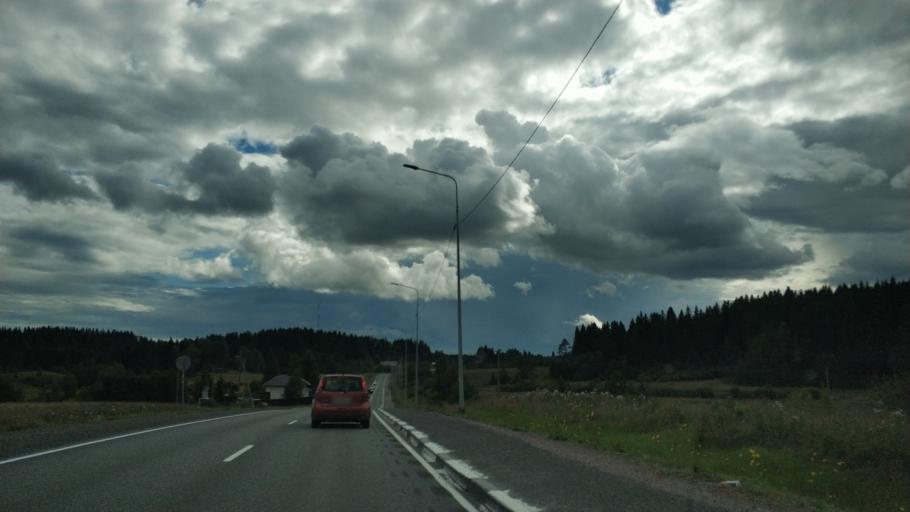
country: RU
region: Republic of Karelia
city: Khelyulya
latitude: 61.7638
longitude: 30.6559
